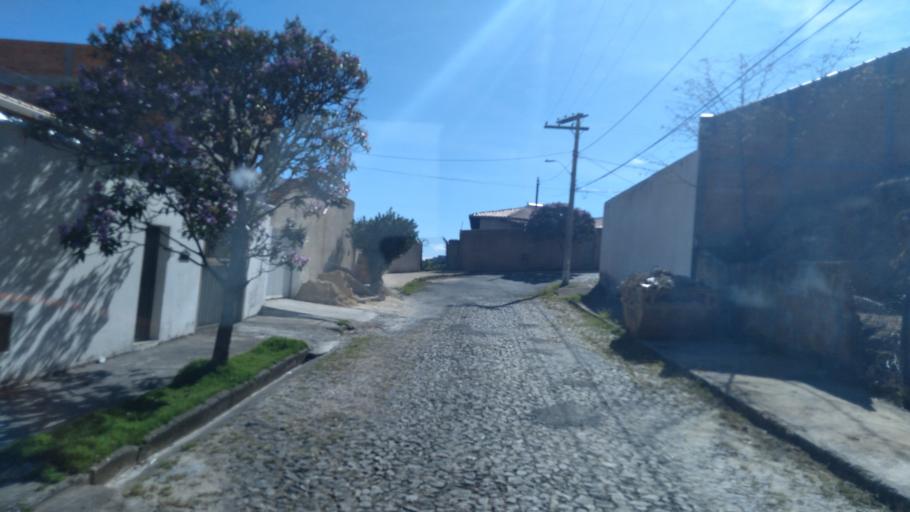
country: BR
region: Minas Gerais
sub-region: Belo Horizonte
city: Belo Horizonte
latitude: -19.9211
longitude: -43.8935
